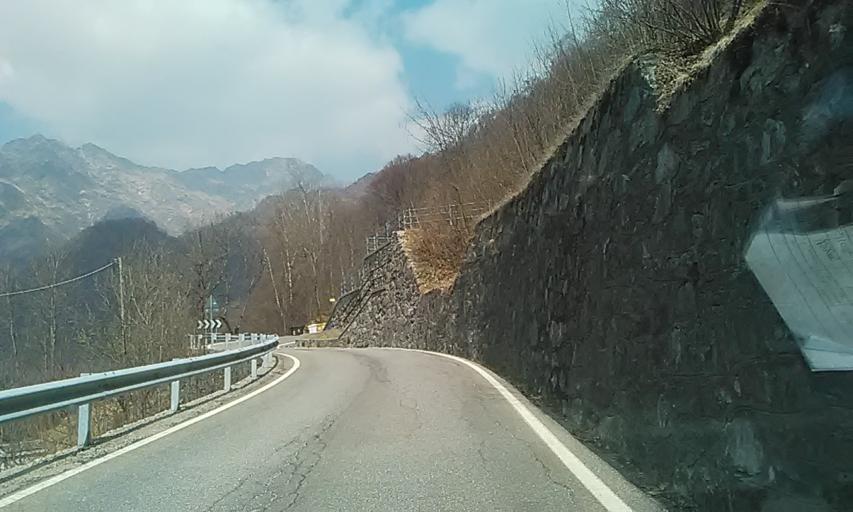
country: IT
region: Piedmont
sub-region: Provincia di Vercelli
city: Rimella
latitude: 45.9118
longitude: 8.1807
